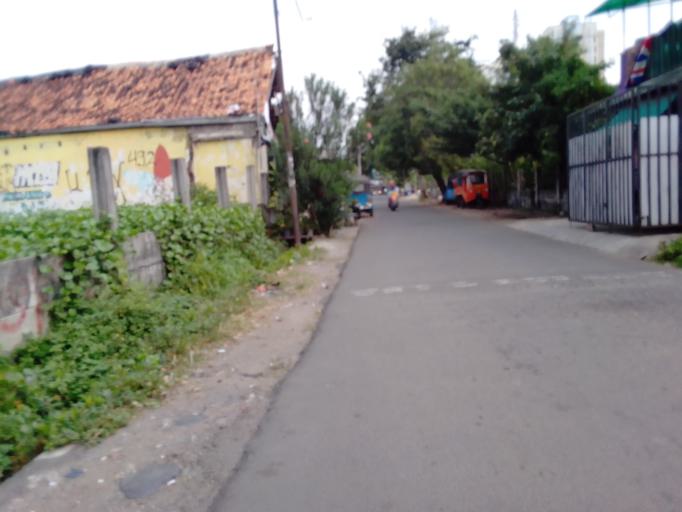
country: ID
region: Jakarta Raya
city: Jakarta
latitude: -6.1645
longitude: 106.8036
